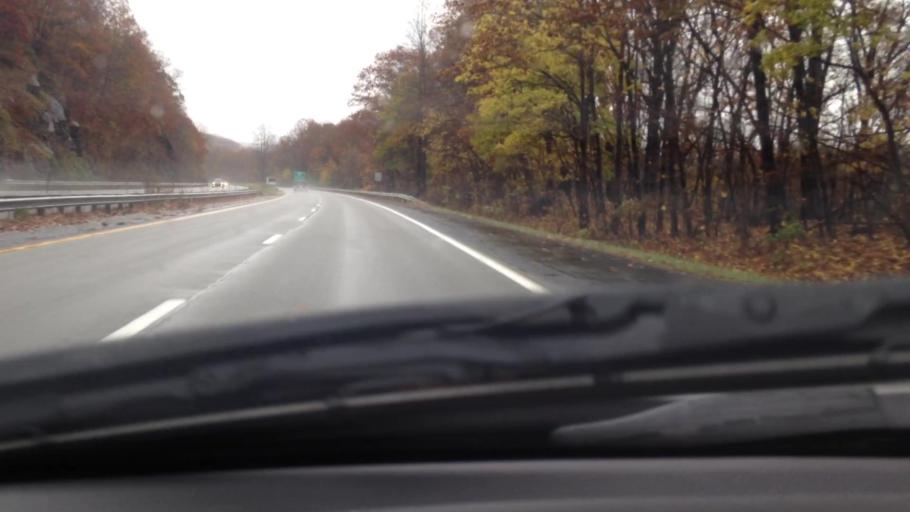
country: US
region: New York
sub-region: Westchester County
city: Montrose
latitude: 41.2516
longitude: -73.9265
